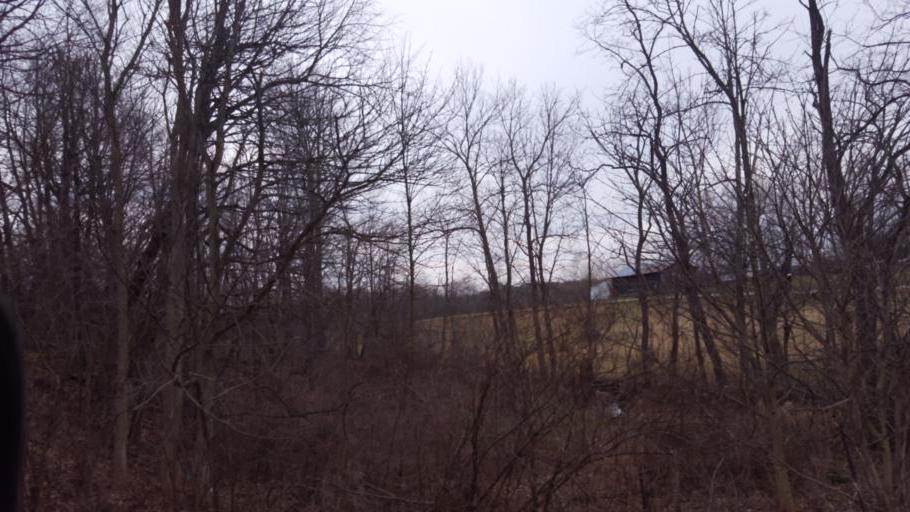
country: US
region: Ohio
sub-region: Richland County
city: Ontario
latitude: 40.8119
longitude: -82.5567
